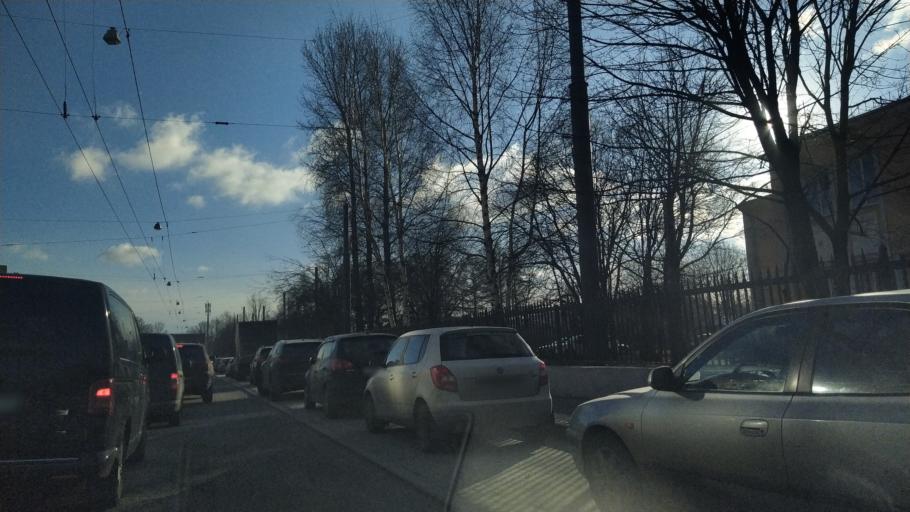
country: RU
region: Leningrad
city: Sampsonievskiy
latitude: 59.9806
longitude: 30.3438
